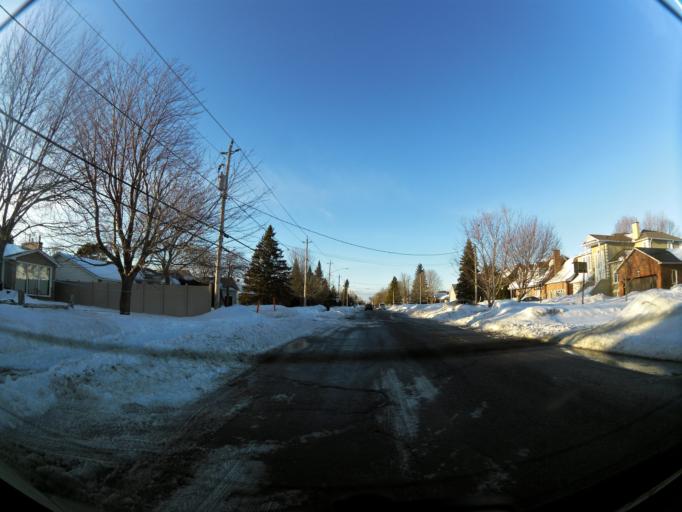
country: CA
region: Ontario
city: Ottawa
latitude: 45.4401
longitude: -75.5236
